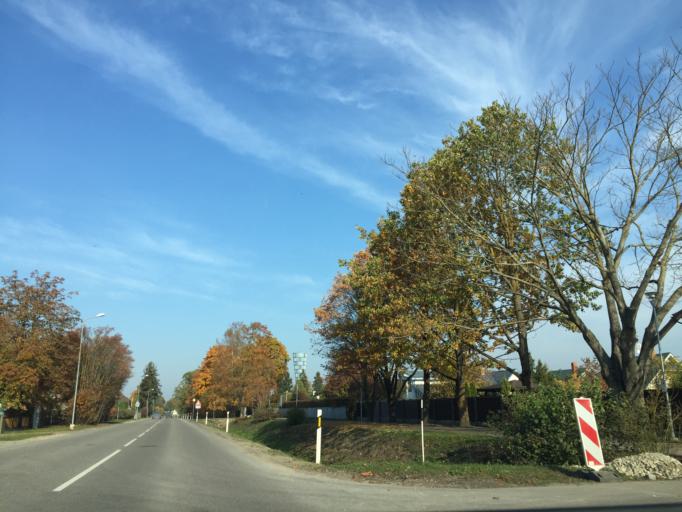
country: LV
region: Marupe
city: Marupe
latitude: 56.8918
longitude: 24.0460
